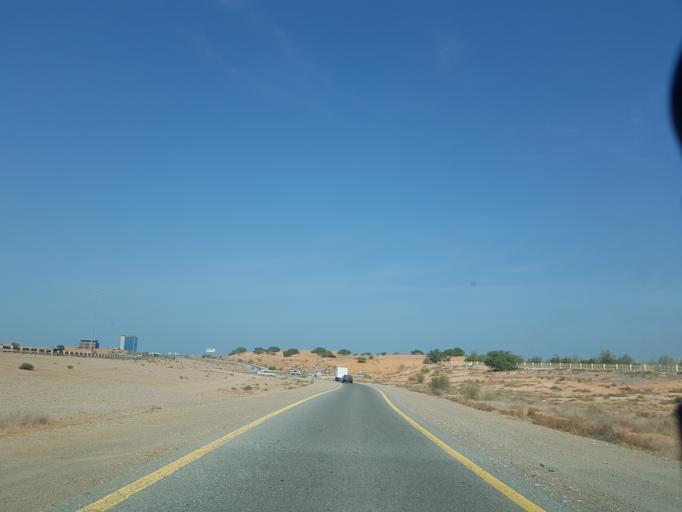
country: AE
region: Ra's al Khaymah
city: Ras al-Khaimah
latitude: 25.6970
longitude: 55.8757
